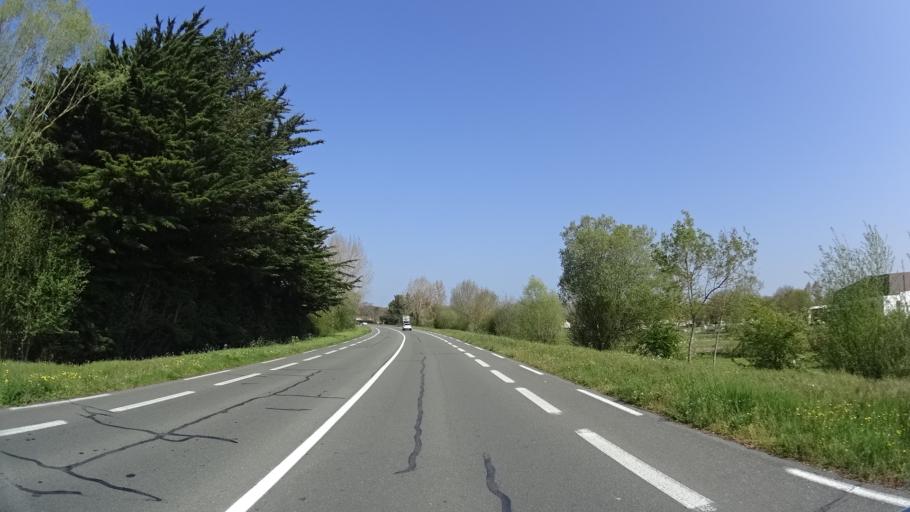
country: FR
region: Pays de la Loire
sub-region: Departement de la Vendee
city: La Barre-de-Monts
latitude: 46.8819
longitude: -2.1215
